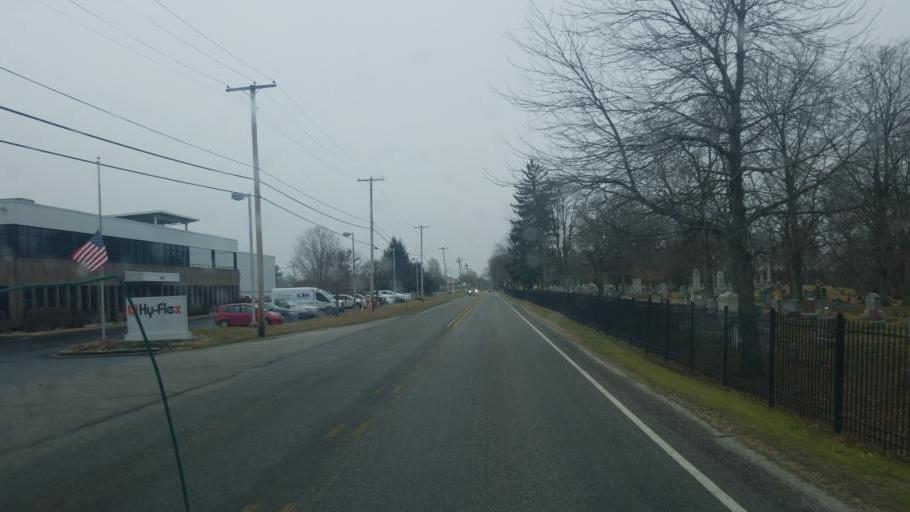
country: US
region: Indiana
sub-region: Henry County
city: Knightstown
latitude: 39.8038
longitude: -85.5323
